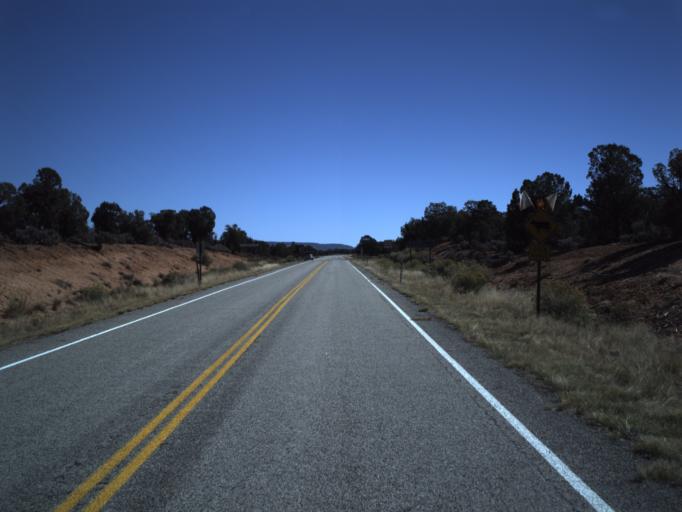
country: US
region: Utah
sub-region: San Juan County
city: Blanding
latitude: 37.5625
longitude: -110.0213
